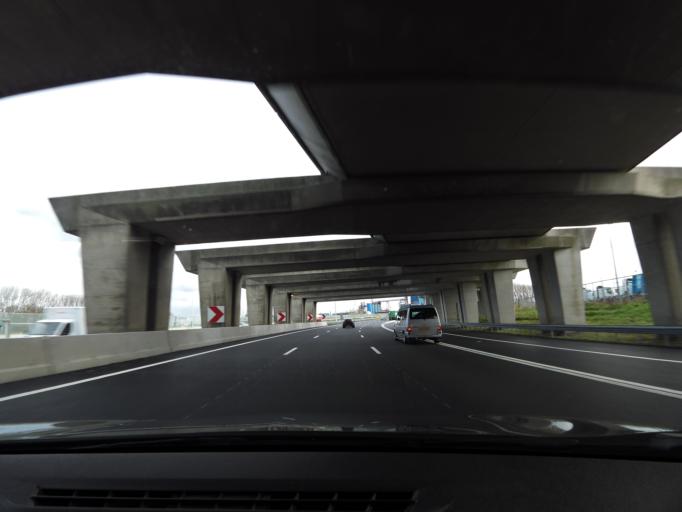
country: NL
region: South Holland
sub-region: Gemeente Maassluis
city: Maassluis
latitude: 51.8959
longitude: 4.2558
